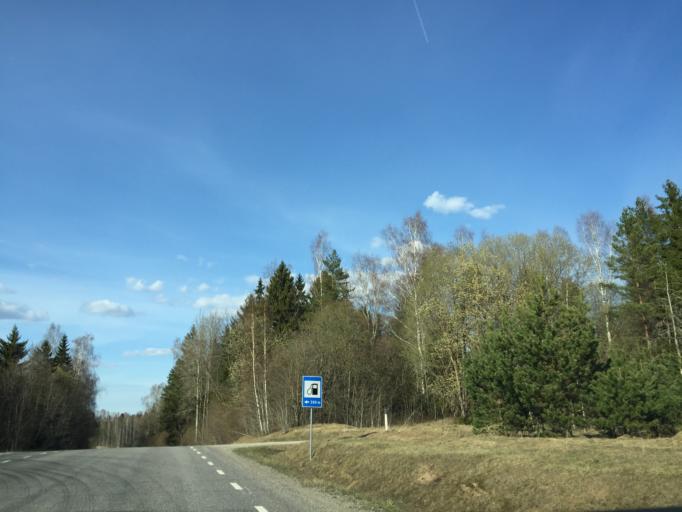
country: EE
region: Tartu
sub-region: Elva linn
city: Elva
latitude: 58.0649
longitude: 26.5161
